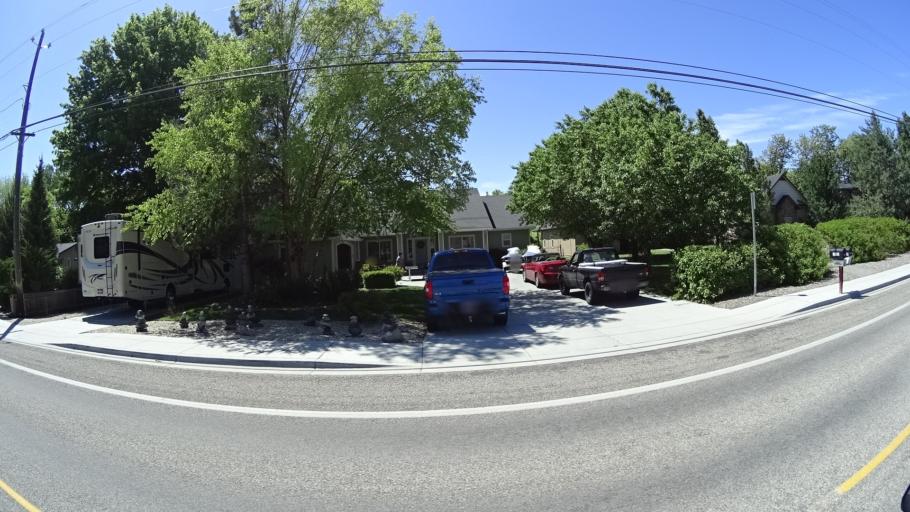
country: US
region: Idaho
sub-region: Ada County
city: Boise
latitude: 43.5641
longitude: -116.1401
